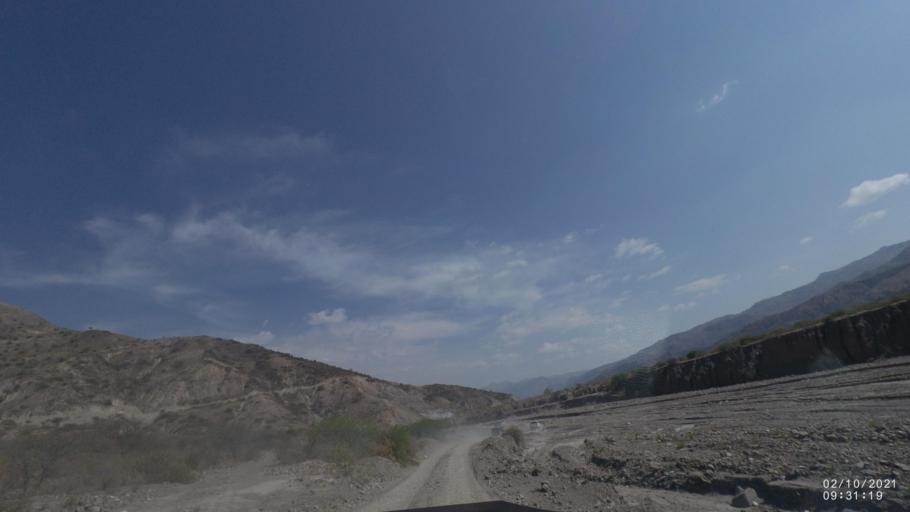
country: BO
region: Cochabamba
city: Irpa Irpa
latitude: -17.8493
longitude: -66.3190
